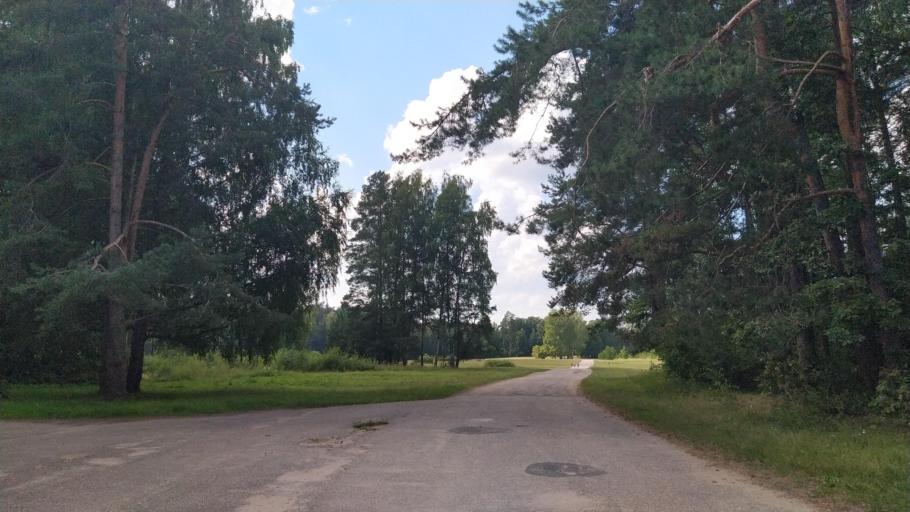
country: RU
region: Pskov
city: Pushkinskiye Gory
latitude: 57.0594
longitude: 28.9315
